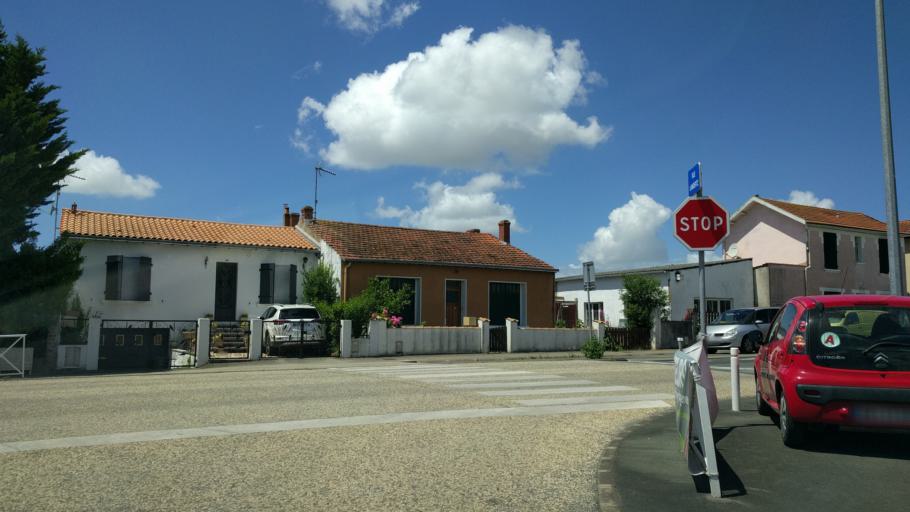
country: FR
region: Poitou-Charentes
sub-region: Departement de la Charente-Maritime
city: Perigny
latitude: 46.1587
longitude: -1.1217
